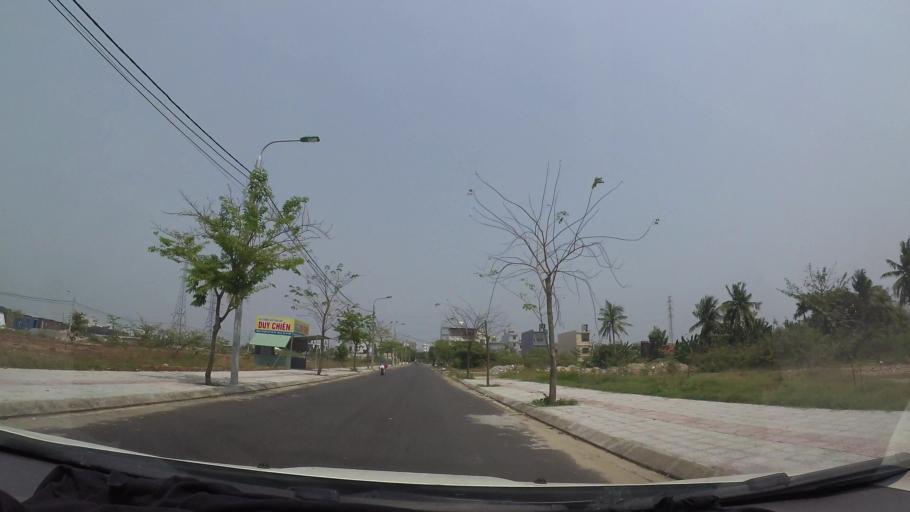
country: VN
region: Da Nang
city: Cam Le
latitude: 16.0201
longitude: 108.2227
